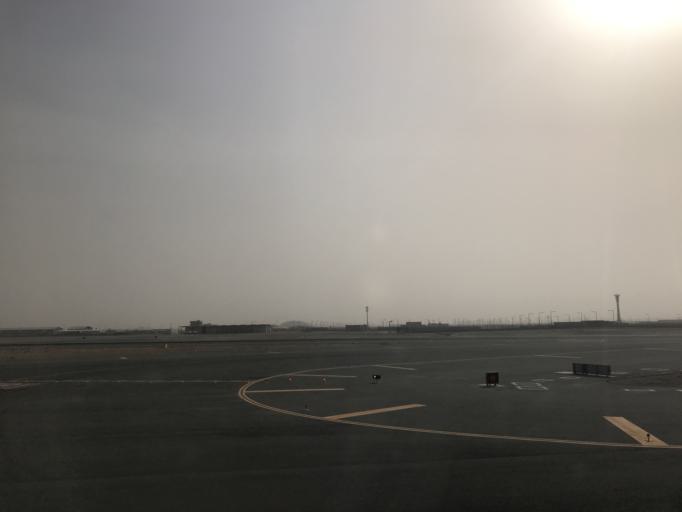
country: QA
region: Baladiyat ad Dawhah
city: Doha
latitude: 25.2770
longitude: 51.5979
